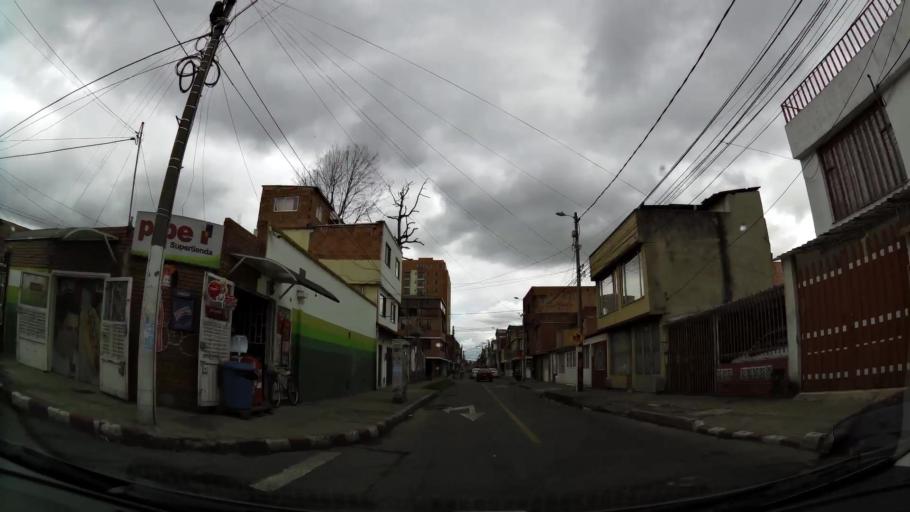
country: CO
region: Bogota D.C.
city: Bogota
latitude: 4.6776
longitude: -74.0980
